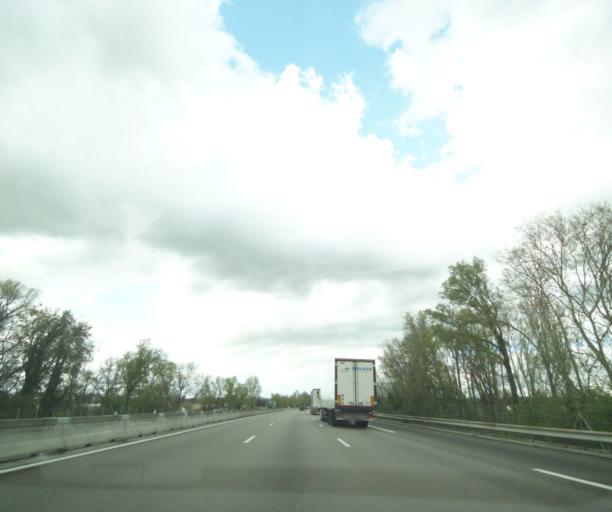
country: FR
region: Rhone-Alpes
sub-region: Departement de la Drome
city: La Roche-de-Glun
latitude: 45.0027
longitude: 4.8759
